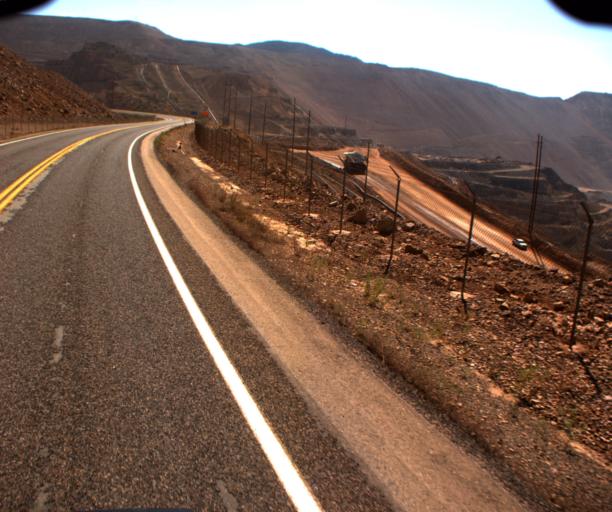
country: US
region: Arizona
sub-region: Greenlee County
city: Morenci
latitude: 33.1211
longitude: -109.3704
